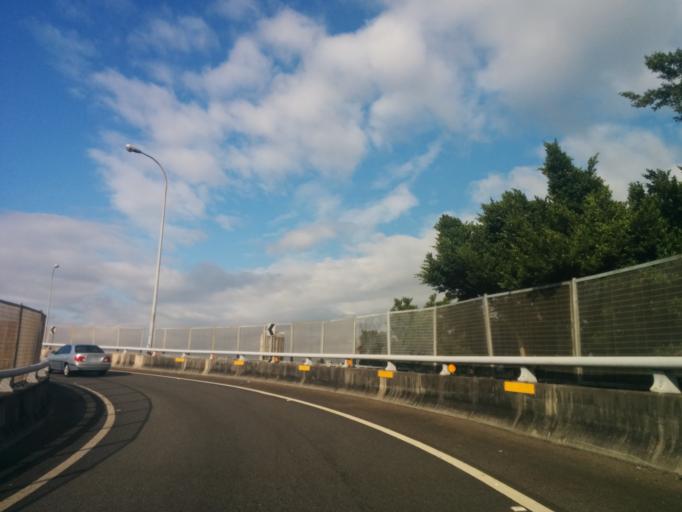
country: TW
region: Taipei
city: Taipei
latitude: 25.0822
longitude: 121.5079
